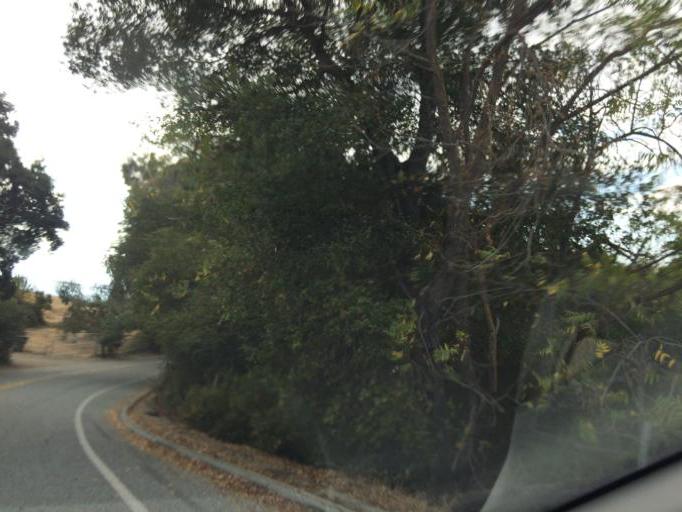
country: US
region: California
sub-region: Santa Clara County
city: East Foothills
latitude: 37.3899
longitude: -121.8049
